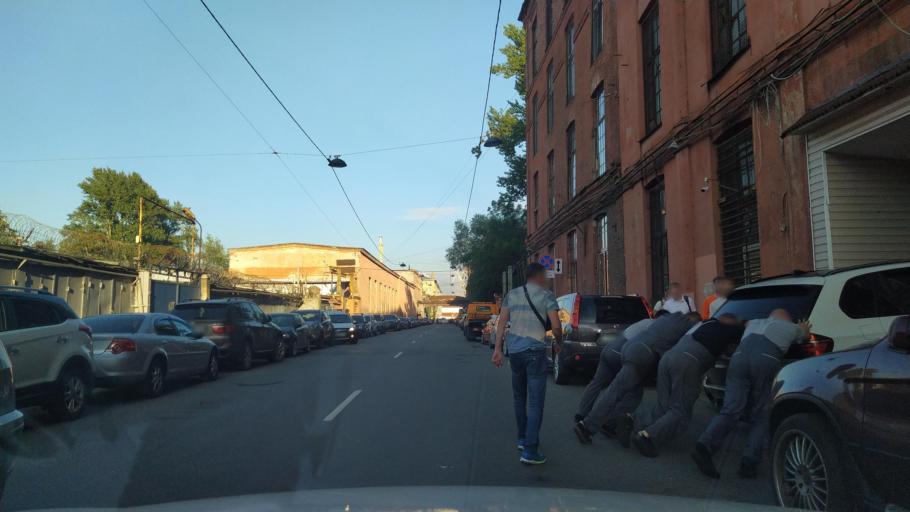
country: RU
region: St.-Petersburg
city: Vasyl'evsky Ostrov
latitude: 59.9234
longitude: 30.2470
